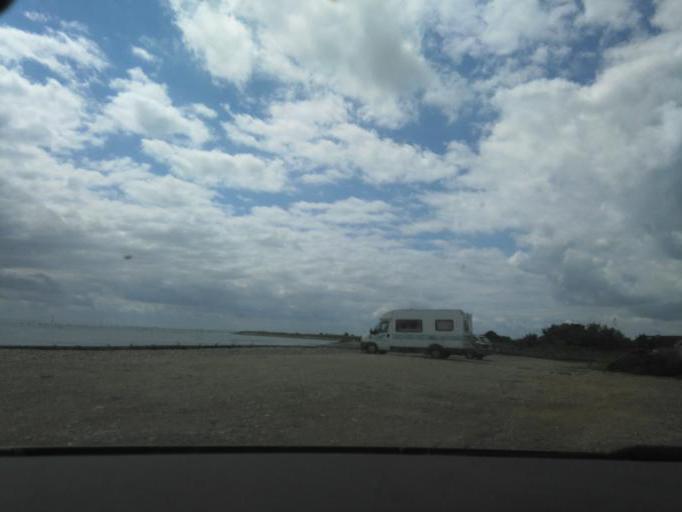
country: DK
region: Zealand
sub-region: Kalundborg Kommune
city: Gorlev
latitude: 55.5166
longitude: 11.1178
